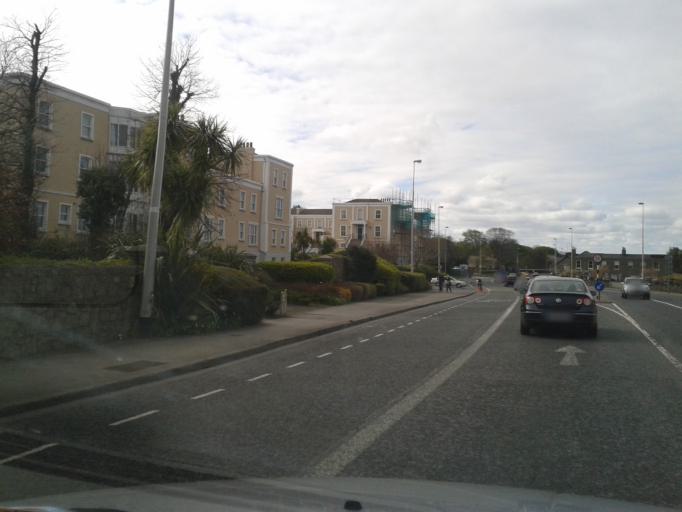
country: IE
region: Leinster
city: Blackrock
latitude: 53.3035
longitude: -6.1846
